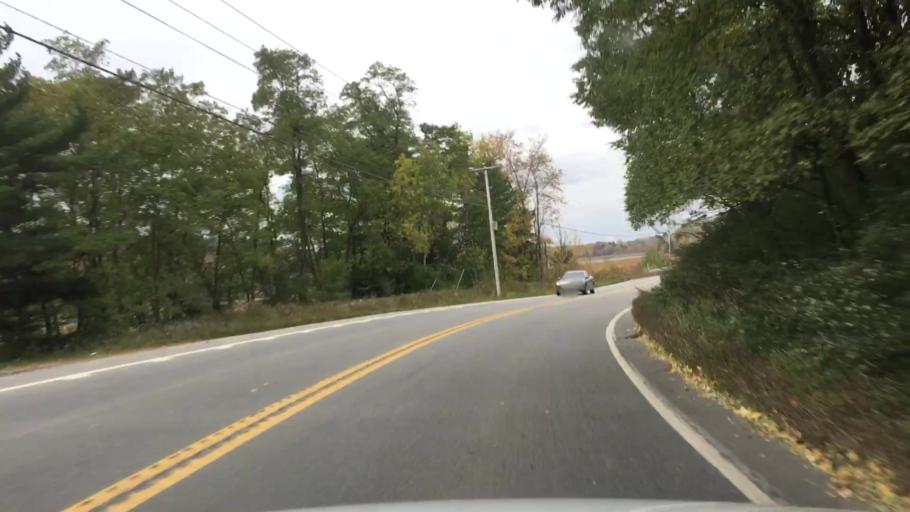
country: US
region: Maine
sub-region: Waldo County
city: Frankfort
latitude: 44.5972
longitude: -68.8656
